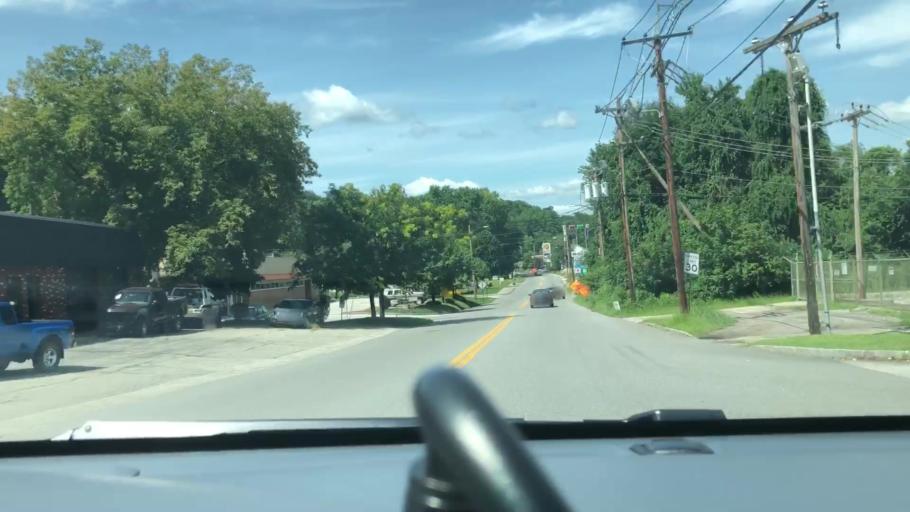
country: US
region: New Hampshire
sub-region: Hillsborough County
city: Manchester
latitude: 42.9971
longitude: -71.4748
